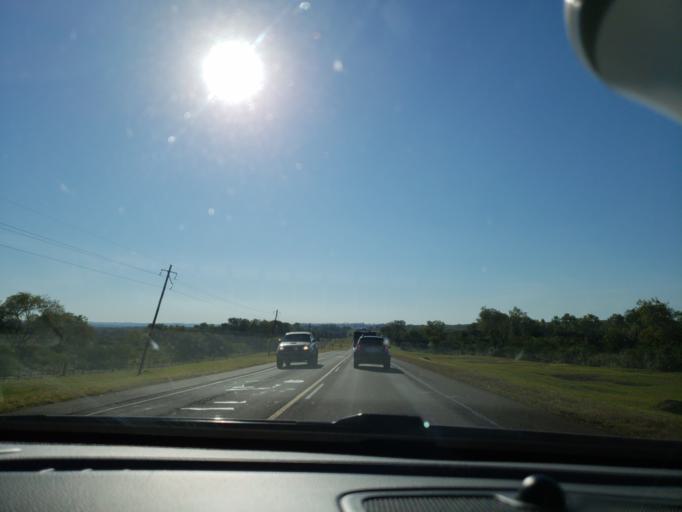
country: AR
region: Misiones
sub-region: Departamento de Apostoles
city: San Jose
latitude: -27.7047
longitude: -55.7990
